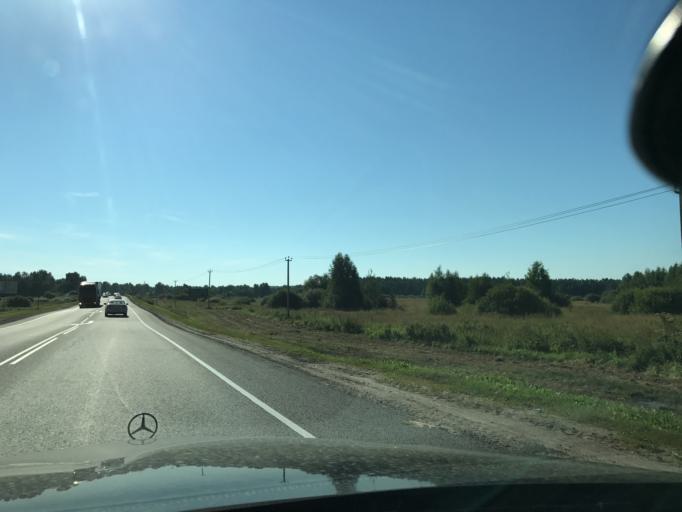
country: RU
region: Moskovskaya
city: Noginsk-9
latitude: 56.1064
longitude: 38.6298
